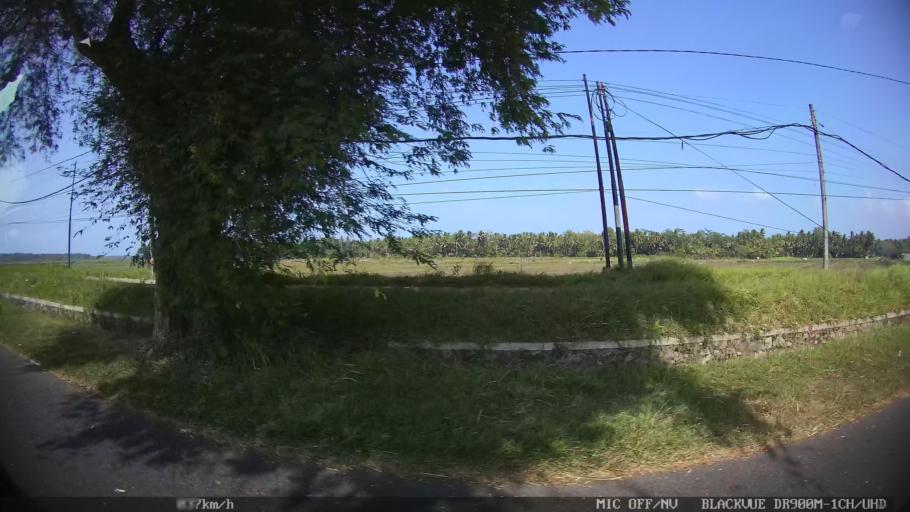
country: ID
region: Daerah Istimewa Yogyakarta
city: Srandakan
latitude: -7.9122
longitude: 110.1764
